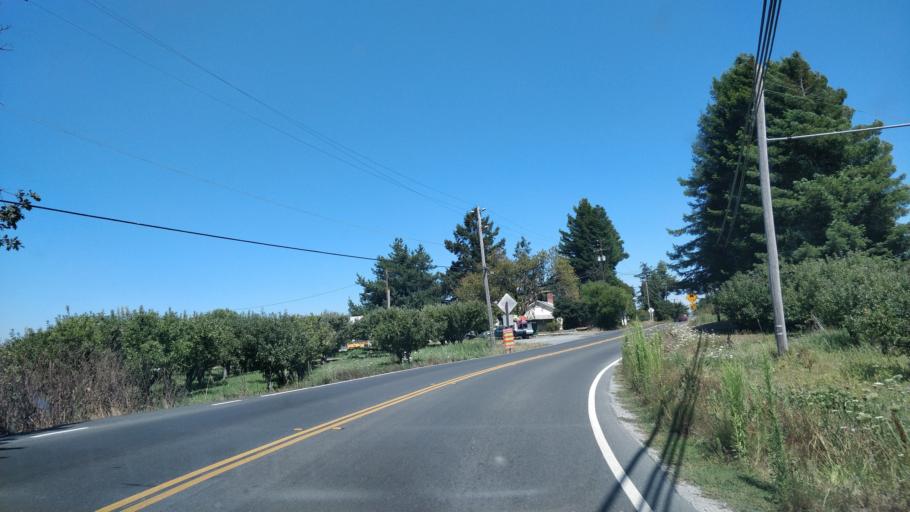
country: US
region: California
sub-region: Sonoma County
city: Sebastopol
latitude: 38.3963
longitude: -122.8607
